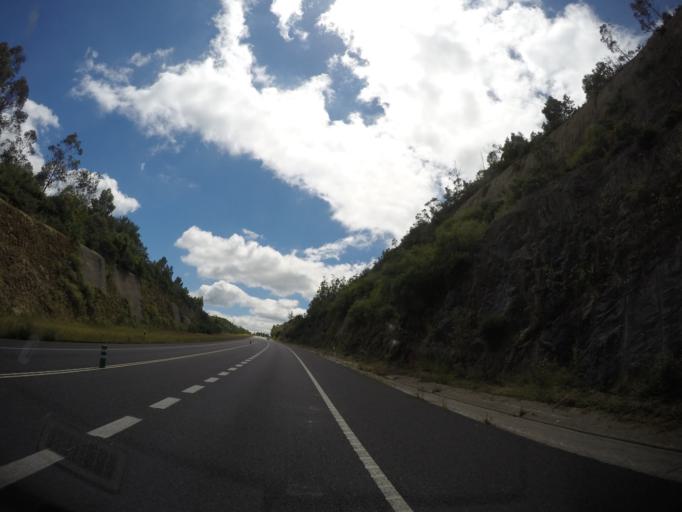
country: ES
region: Aragon
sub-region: Provincia de Zaragoza
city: El Burgo de Ebro
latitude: 41.5482
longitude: -0.7469
